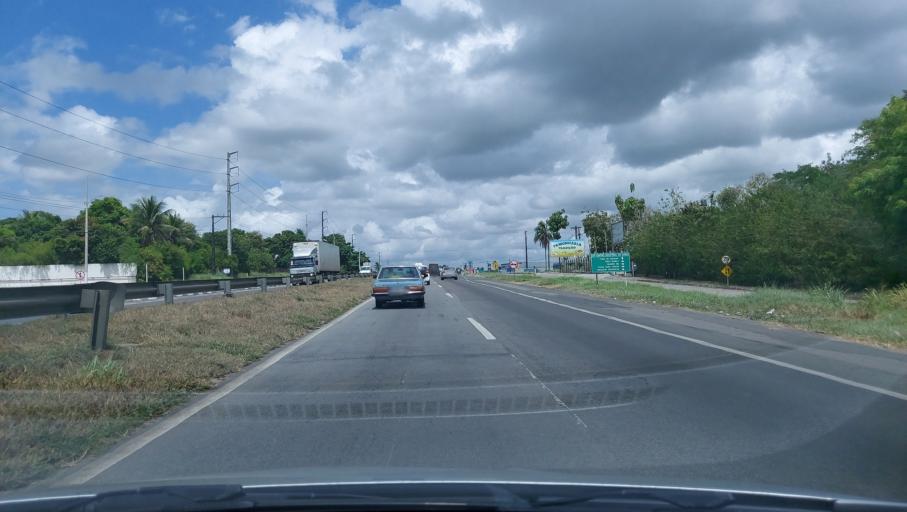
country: BR
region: Bahia
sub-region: Conceicao Do Jacuipe
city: Conceicao do Jacuipe
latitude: -12.3352
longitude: -38.8523
